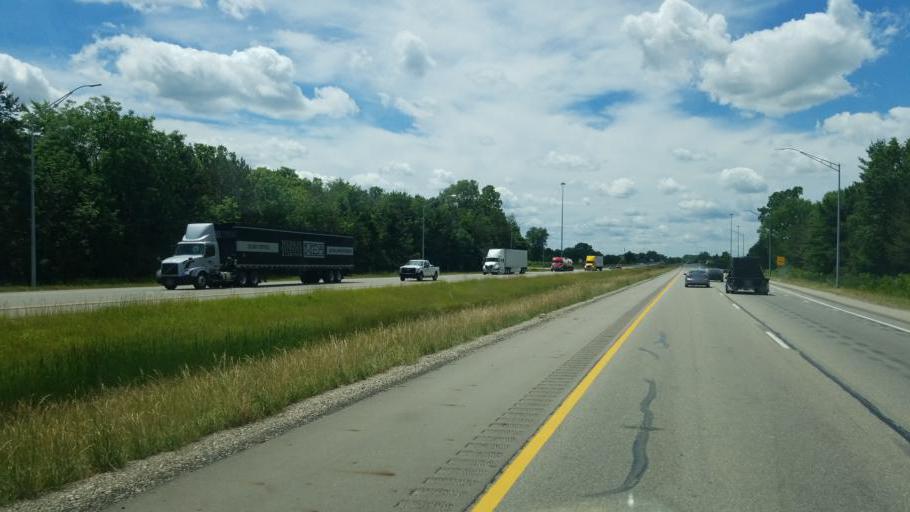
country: US
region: Michigan
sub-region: Ingham County
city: Holt
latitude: 42.6638
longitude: -84.5258
